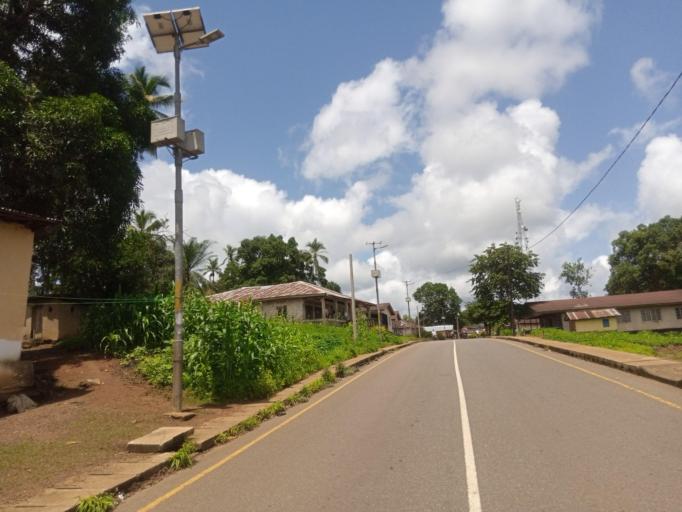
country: SL
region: Northern Province
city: Port Loko
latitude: 8.7684
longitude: -12.7872
